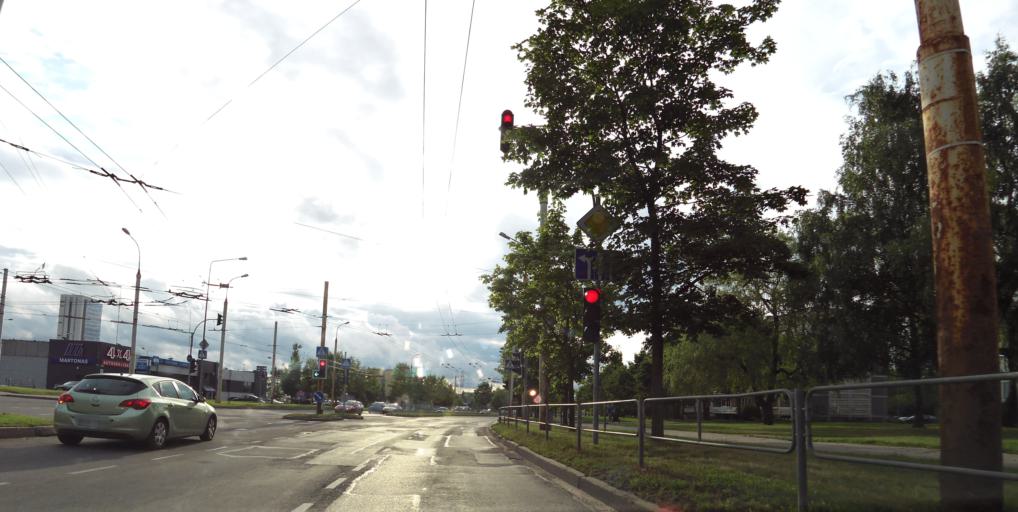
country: LT
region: Vilnius County
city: Justiniskes
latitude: 54.7038
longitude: 25.2192
